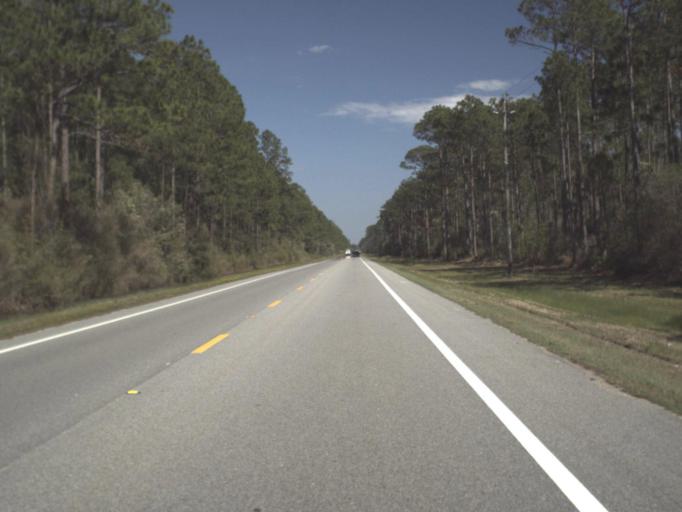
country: US
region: Florida
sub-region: Bay County
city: Lynn Haven
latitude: 30.3221
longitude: -85.6848
